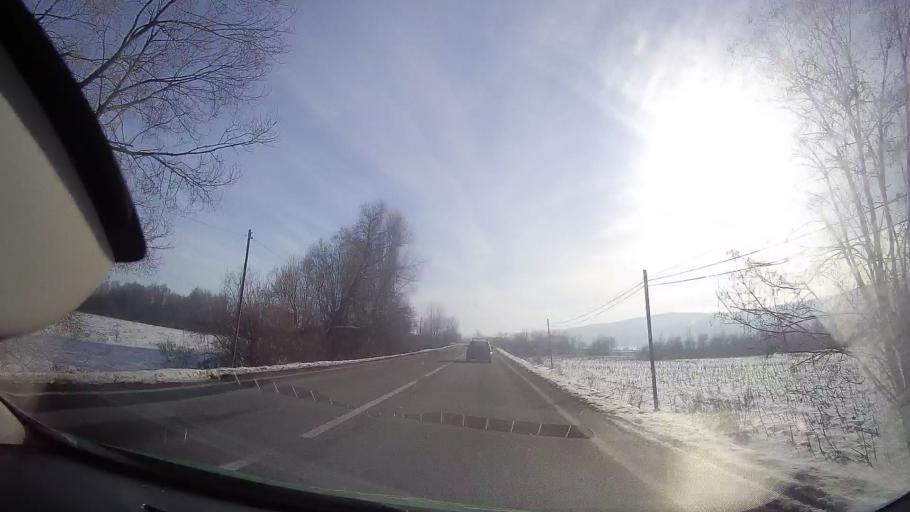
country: RO
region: Neamt
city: Bodesti
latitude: 47.0490
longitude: 26.4036
